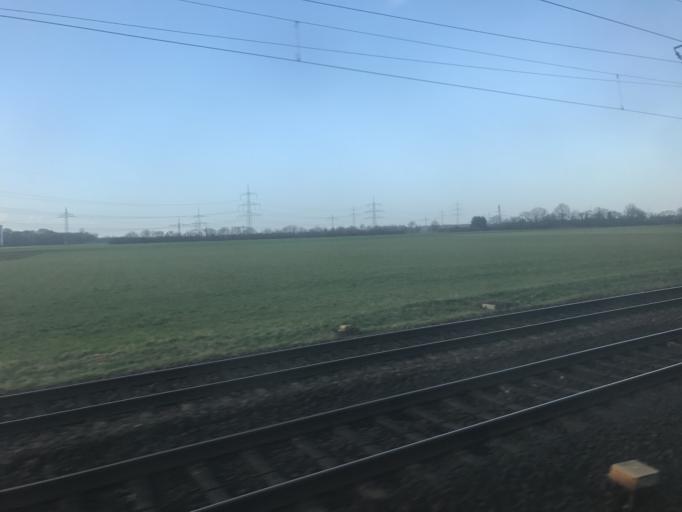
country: DE
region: North Rhine-Westphalia
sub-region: Regierungsbezirk Dusseldorf
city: Langenfeld
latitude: 51.0725
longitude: 6.9567
